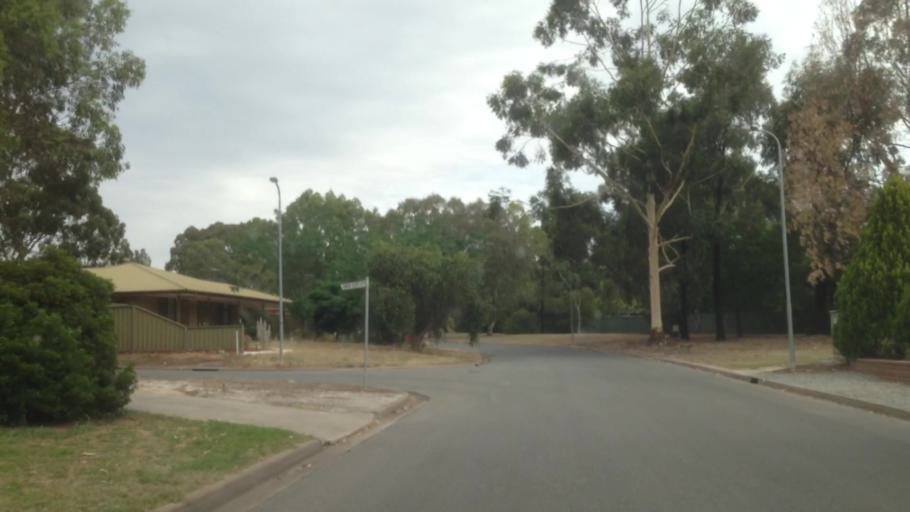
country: AU
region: South Australia
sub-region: Barossa
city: Williamstown
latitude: -34.6697
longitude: 138.8798
